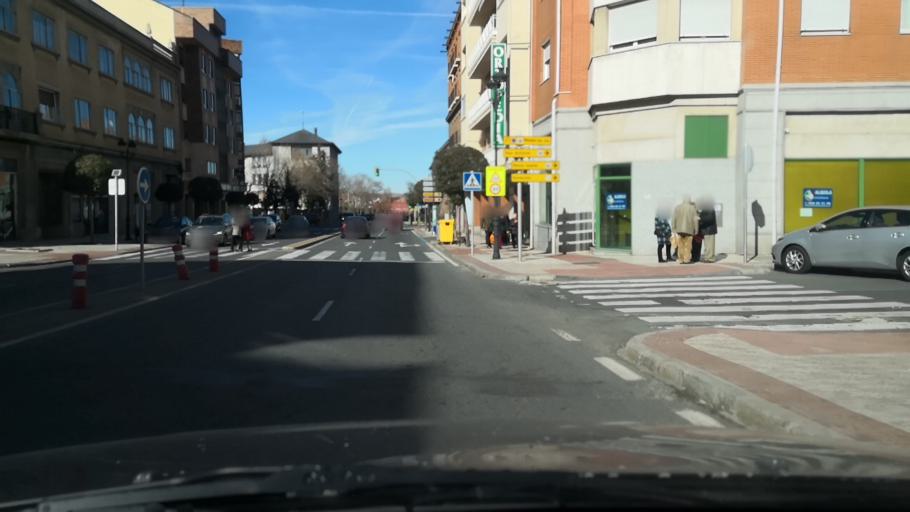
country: ES
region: Castille and Leon
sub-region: Provincia de Avila
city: Avila
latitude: 40.6558
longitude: -4.6870
